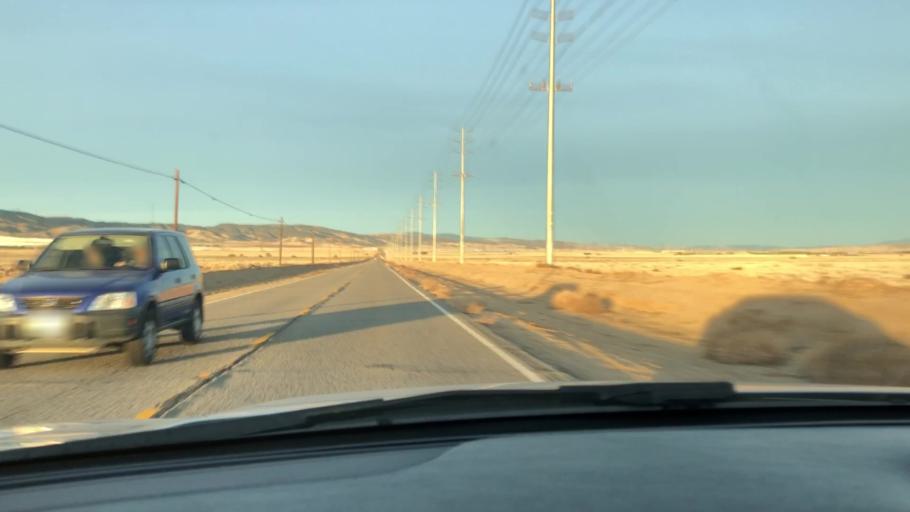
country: US
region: California
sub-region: Los Angeles County
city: Quartz Hill
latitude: 34.6749
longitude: -118.2580
